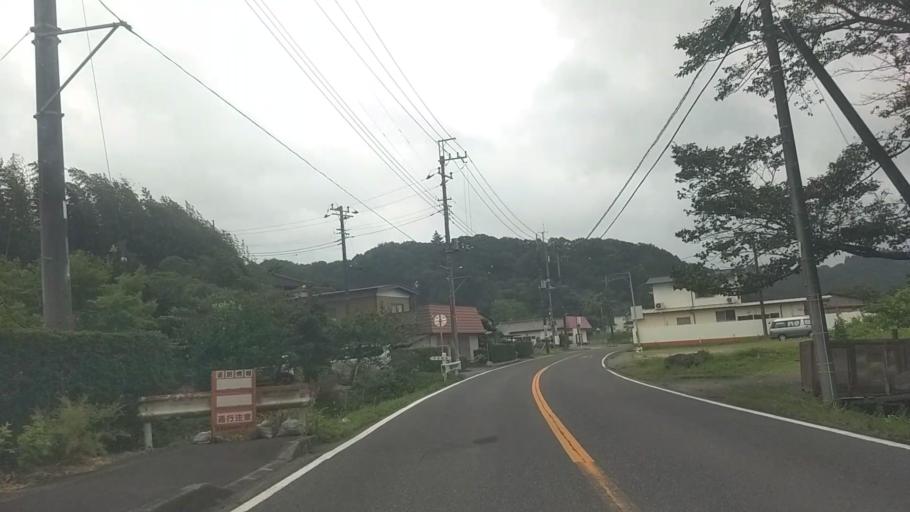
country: JP
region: Chiba
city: Kawaguchi
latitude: 35.2602
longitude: 140.0639
